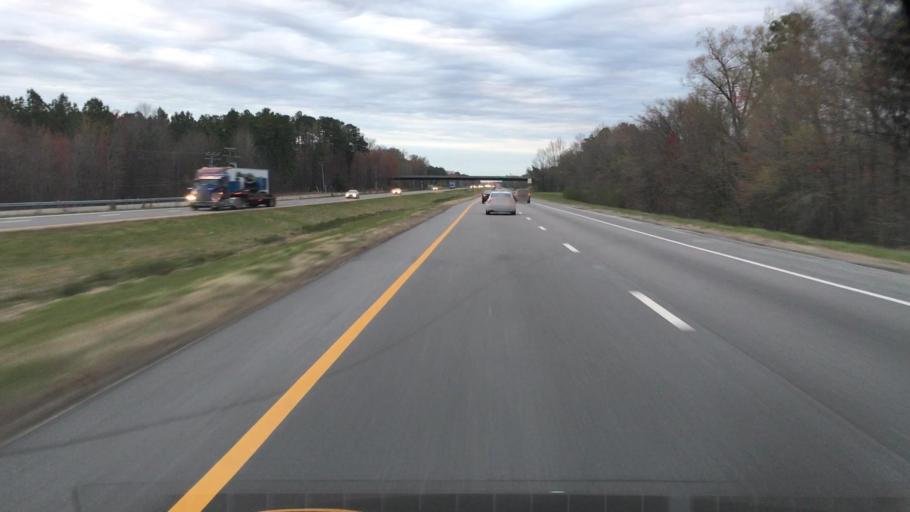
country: US
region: Virginia
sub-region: Sussex County
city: Sussex
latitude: 36.9009
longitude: -77.3997
